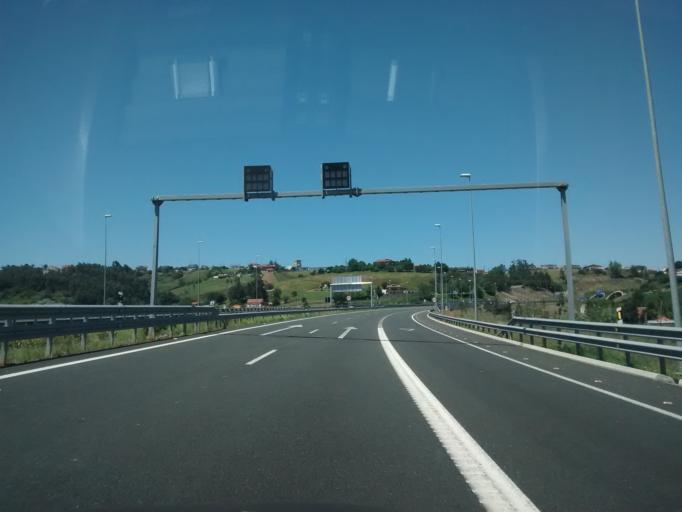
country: ES
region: Cantabria
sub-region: Provincia de Cantabria
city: Camargo
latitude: 43.3864
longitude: -3.8619
